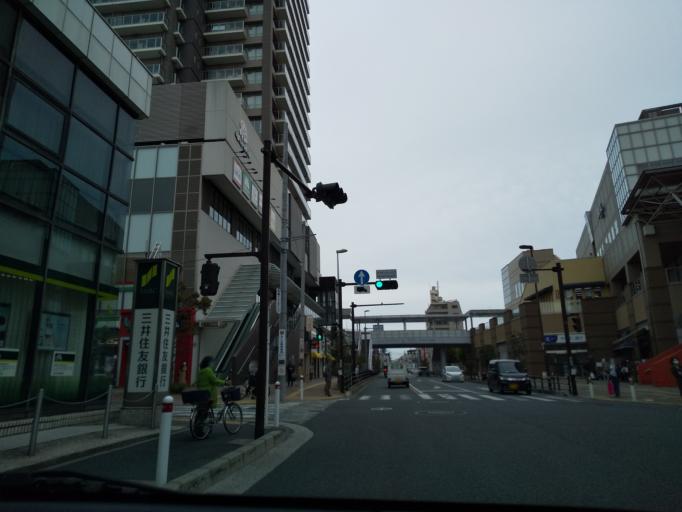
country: JP
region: Tokyo
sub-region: Machida-shi
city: Machida
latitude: 35.5150
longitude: 139.4214
